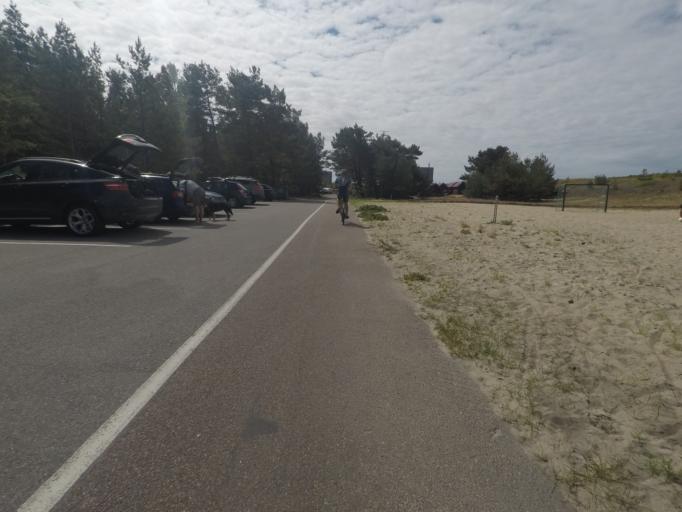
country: LT
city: Neringa
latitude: 55.5406
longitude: 21.1000
